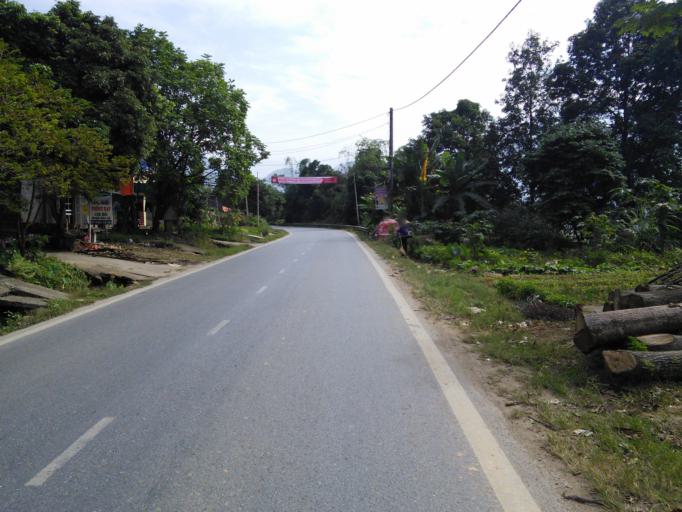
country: VN
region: Lao Cai
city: Lao Cai
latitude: 22.4626
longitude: 103.9476
